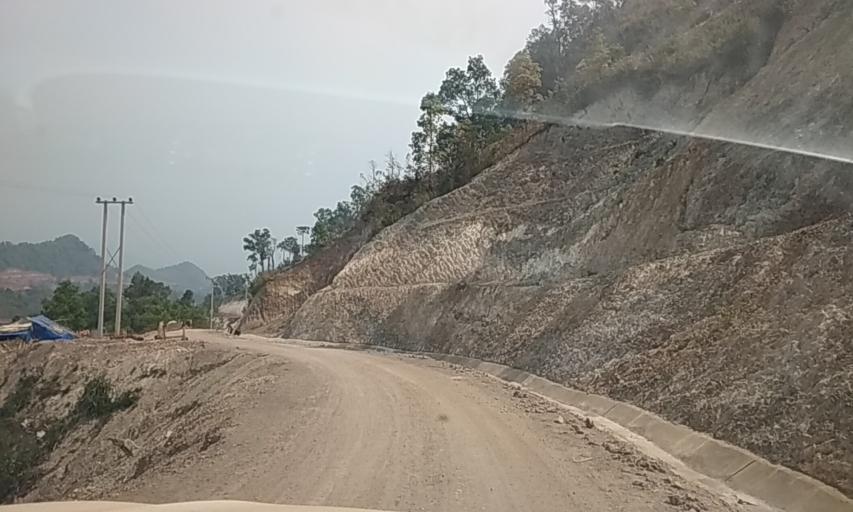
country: VN
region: Huyen Dien Bien
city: Dien Bien Phu
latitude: 21.4848
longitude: 102.7818
